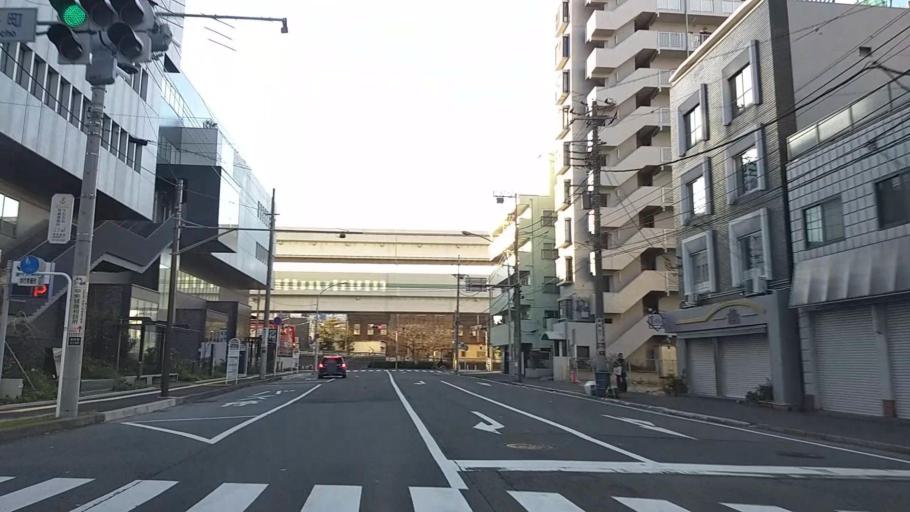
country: JP
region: Kanagawa
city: Yokohama
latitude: 35.4346
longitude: 139.6269
